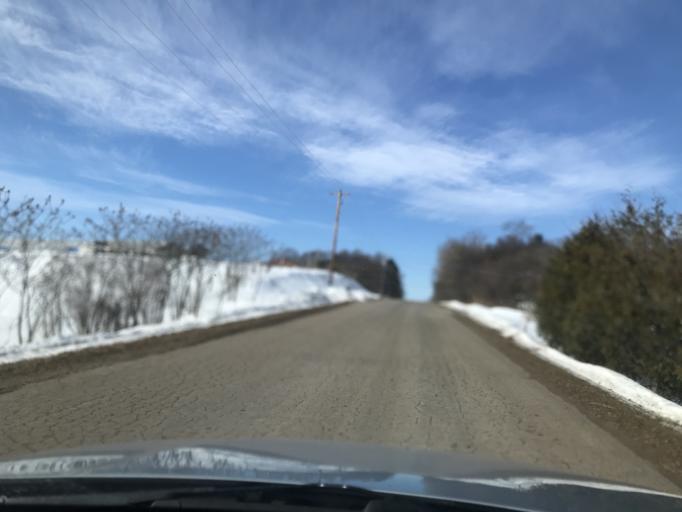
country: US
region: Wisconsin
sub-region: Oconto County
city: Gillett
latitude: 44.9618
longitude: -88.2978
